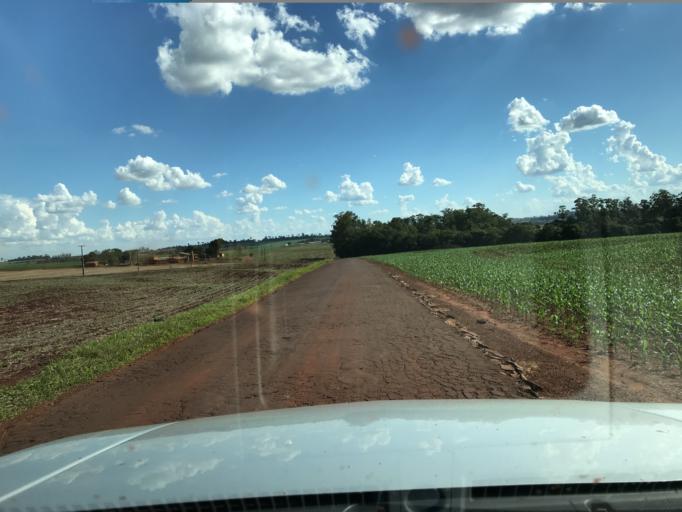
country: BR
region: Parana
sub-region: Palotina
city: Palotina
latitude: -24.2444
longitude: -53.7912
